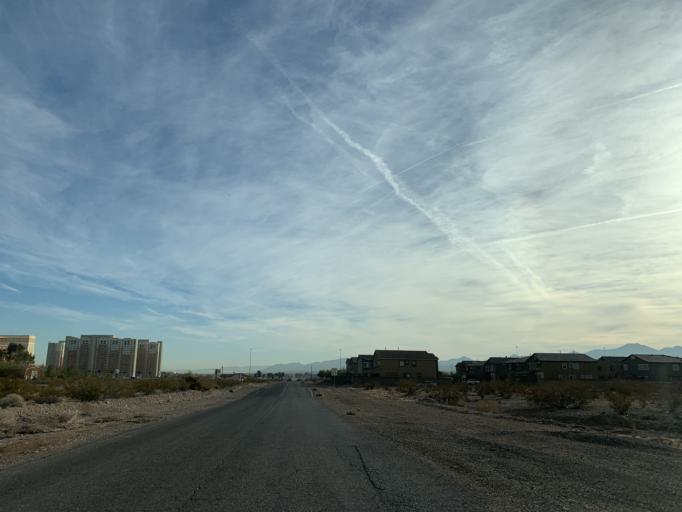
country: US
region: Nevada
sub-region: Clark County
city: Enterprise
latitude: 36.0062
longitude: -115.1870
